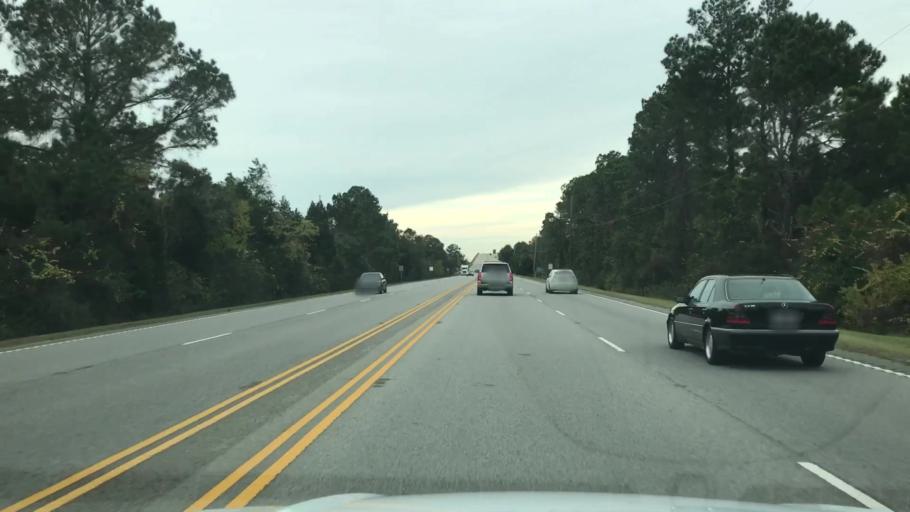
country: US
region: South Carolina
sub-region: Georgetown County
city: Georgetown
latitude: 33.3648
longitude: -79.2436
